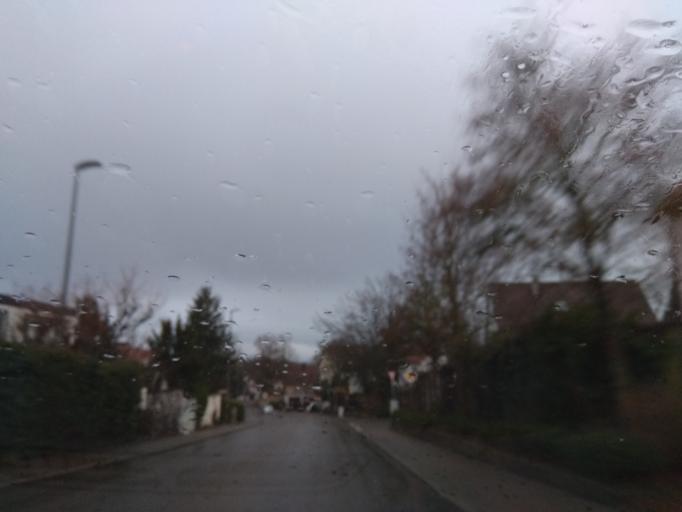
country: DE
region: Baden-Wuerttemberg
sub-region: Regierungsbezirk Stuttgart
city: Steinenbronn
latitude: 48.6933
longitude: 9.1252
